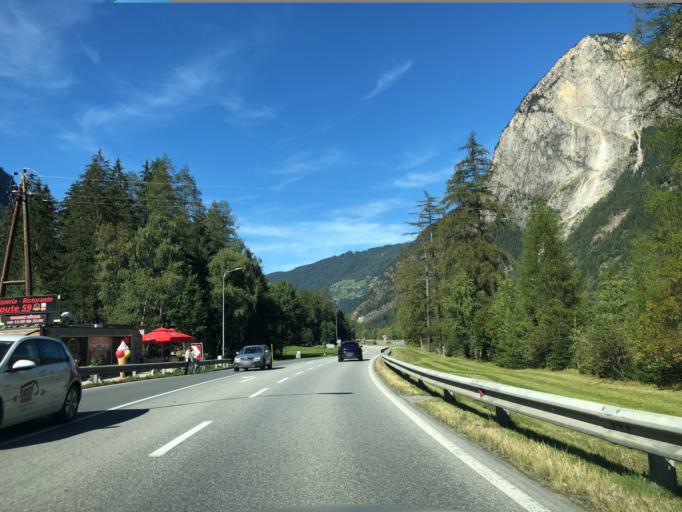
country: AT
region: Tyrol
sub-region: Politischer Bezirk Imst
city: Oetz
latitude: 47.1644
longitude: 10.9104
